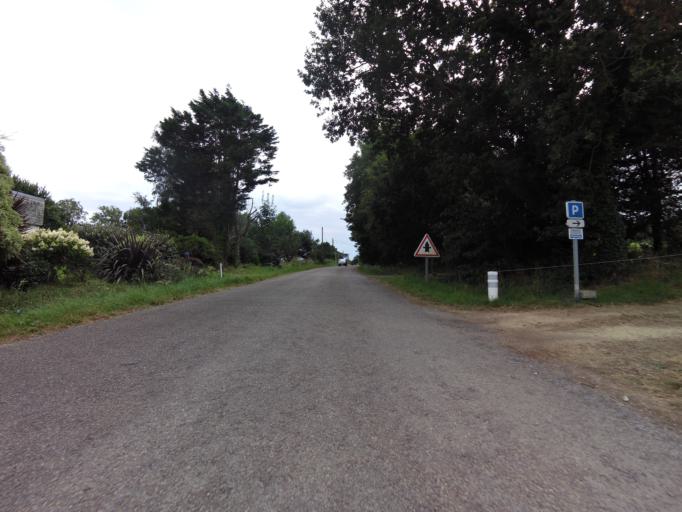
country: FR
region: Brittany
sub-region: Departement du Finistere
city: Beuzec-Cap-Sizun
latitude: 48.0936
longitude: -4.4670
